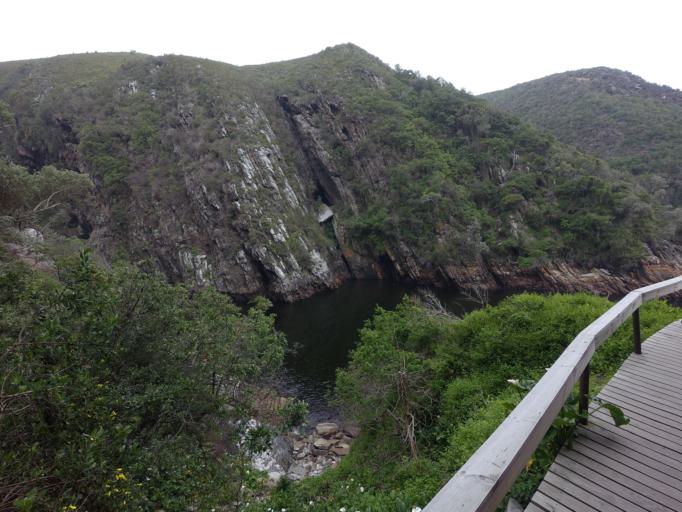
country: ZA
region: Eastern Cape
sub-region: Cacadu District Municipality
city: Kareedouw
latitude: -34.0189
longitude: 23.9035
